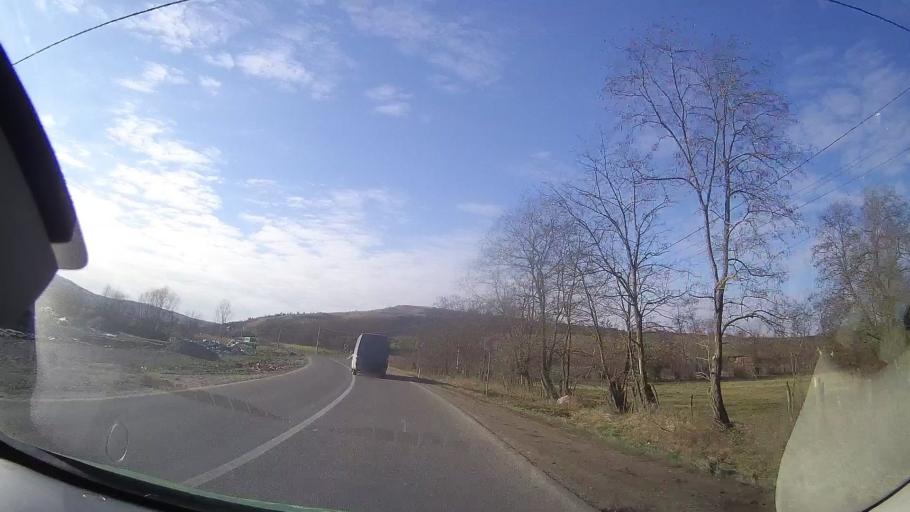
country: RO
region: Cluj
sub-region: Comuna Caianu
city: Caianu
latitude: 46.8021
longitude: 23.9306
